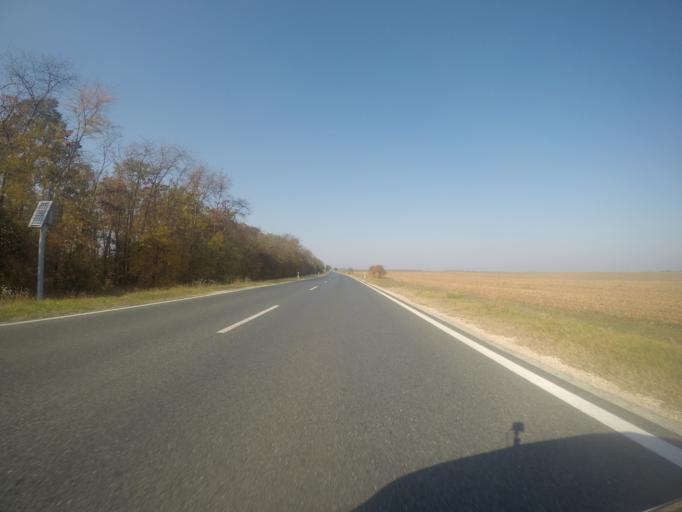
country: HU
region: Tolna
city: Madocsa
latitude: 46.7065
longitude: 18.8883
